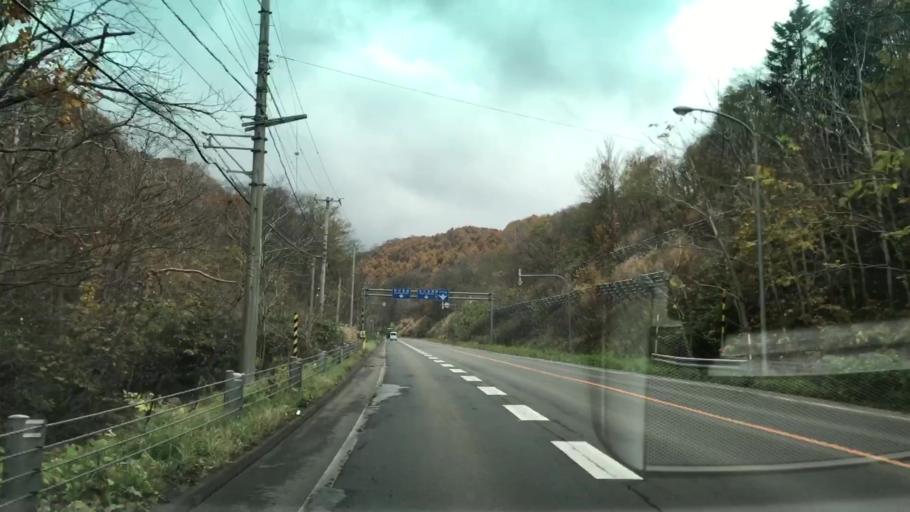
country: JP
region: Hokkaido
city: Yoichi
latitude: 43.2279
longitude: 140.7345
